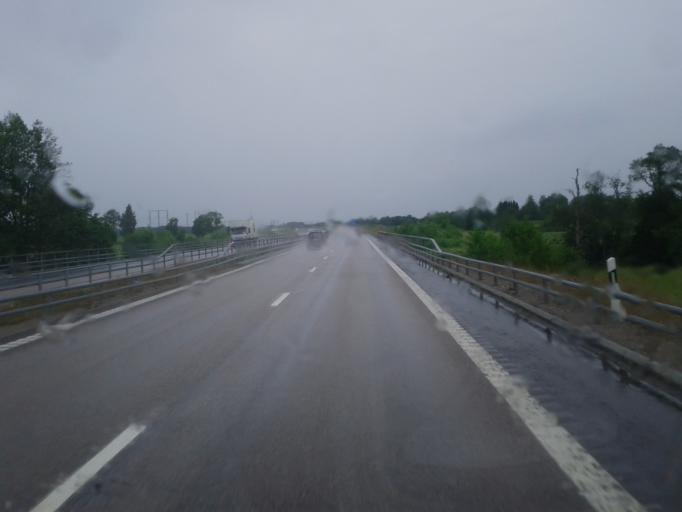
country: SE
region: Uppsala
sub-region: Tierps Kommun
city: Tierp
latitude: 60.3248
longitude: 17.5114
